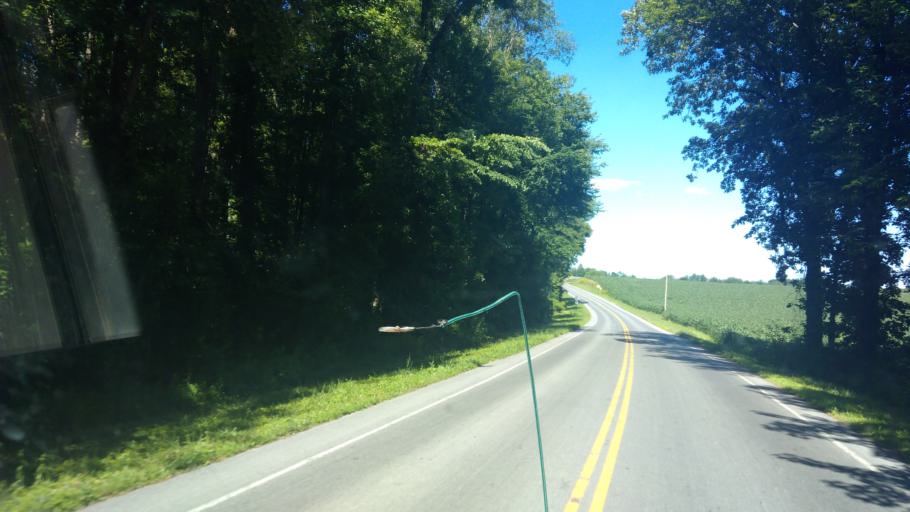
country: US
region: New York
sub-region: Wayne County
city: Lyons
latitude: 43.0215
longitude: -76.9376
